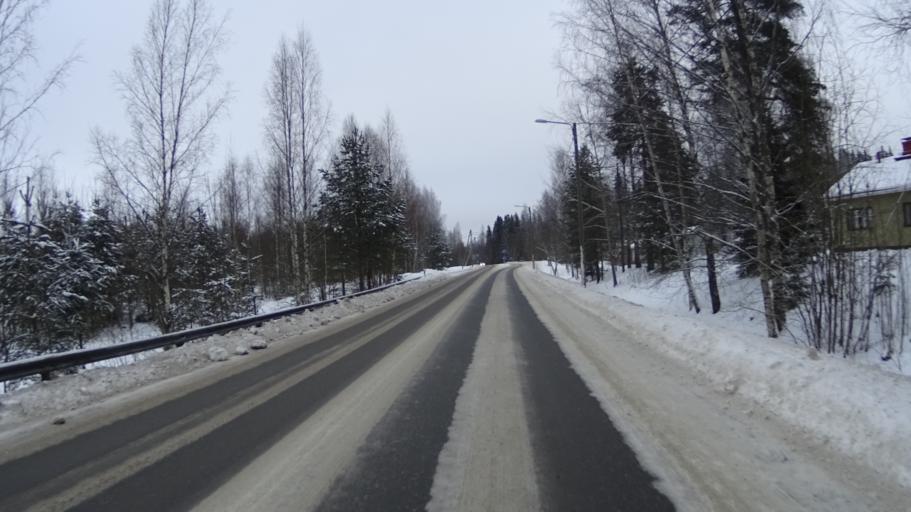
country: FI
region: Uusimaa
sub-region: Helsinki
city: Karkkila
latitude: 60.5246
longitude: 24.2040
